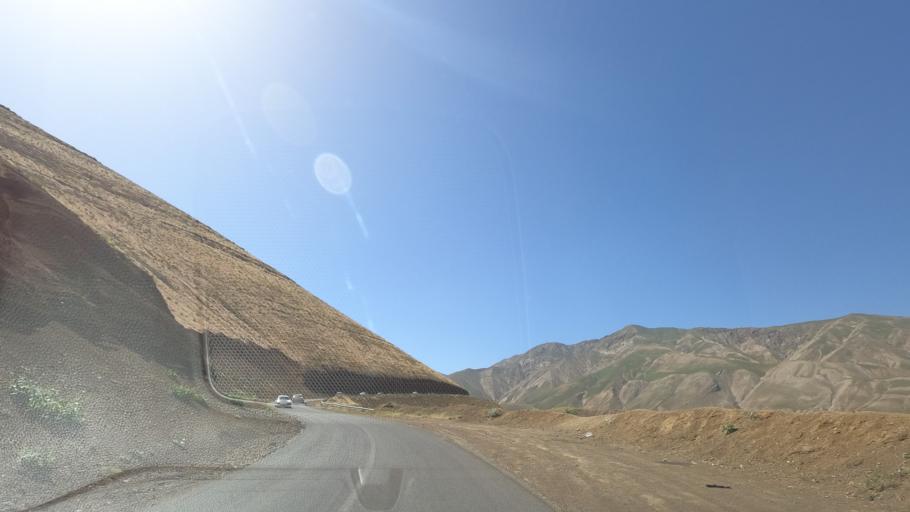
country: IR
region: Alborz
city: Karaj
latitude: 35.9354
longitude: 51.0811
